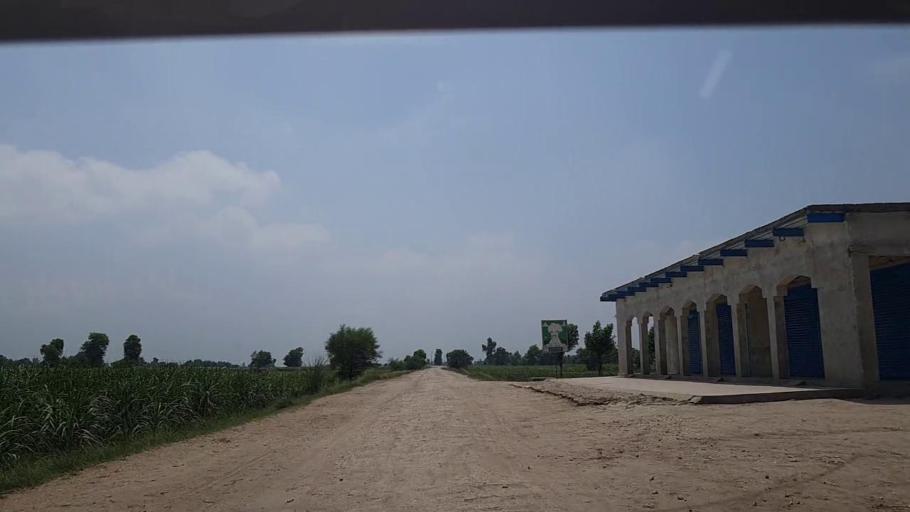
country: PK
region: Sindh
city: Khanpur
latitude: 27.9116
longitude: 69.3944
